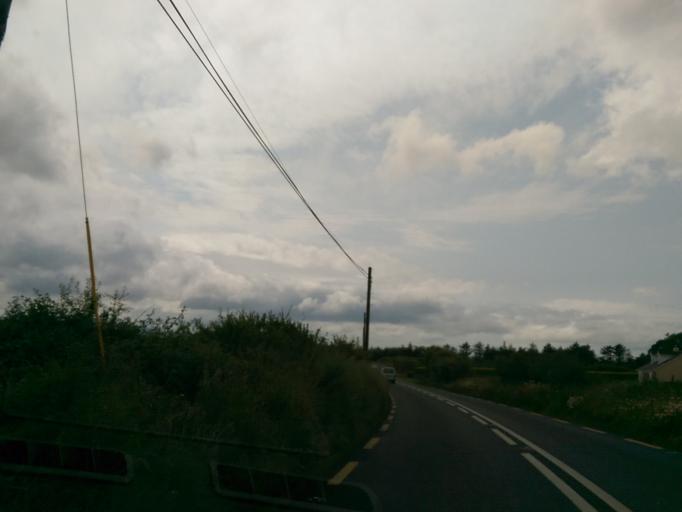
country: IE
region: Munster
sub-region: An Clar
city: Kilrush
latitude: 52.6524
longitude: -9.4543
